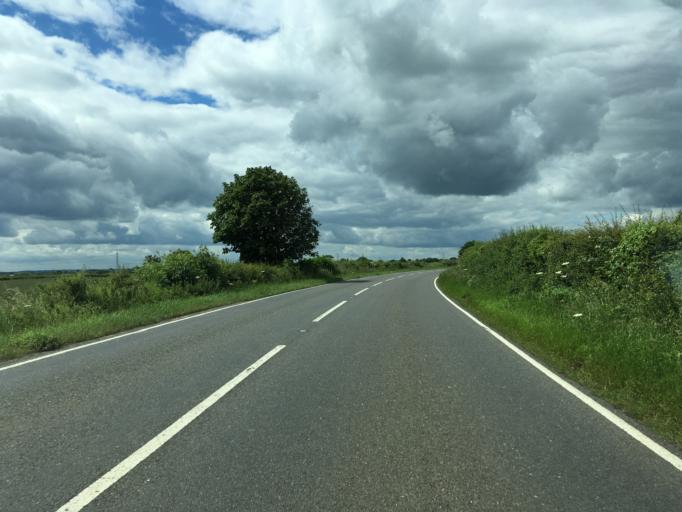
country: GB
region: England
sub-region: Oxfordshire
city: Adderbury
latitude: 52.0865
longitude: -1.2560
